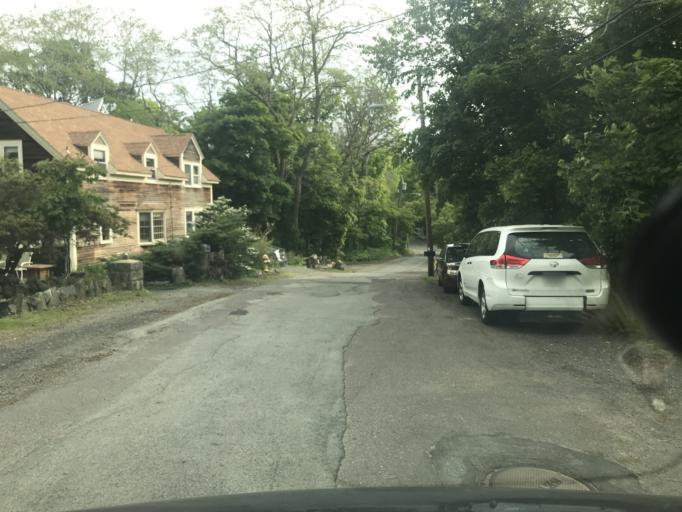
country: US
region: Massachusetts
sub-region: Essex County
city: Rockport
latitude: 42.6806
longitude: -70.6324
